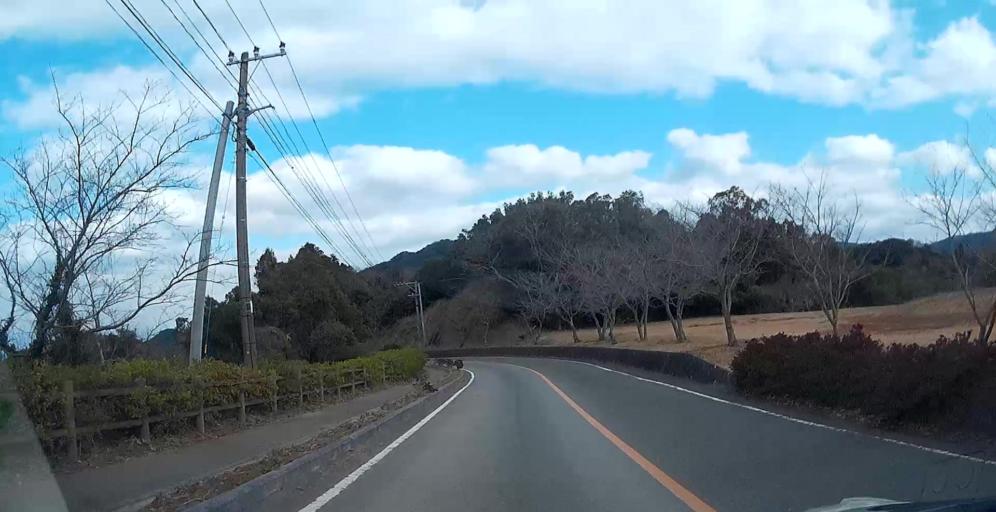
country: JP
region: Kumamoto
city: Yatsushiro
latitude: 32.3715
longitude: 130.5022
